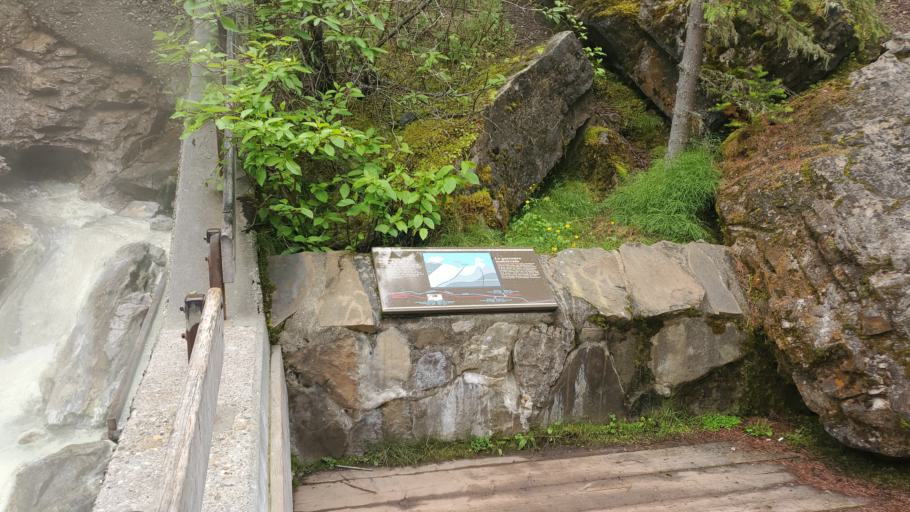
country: CA
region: Alberta
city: Hinton
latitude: 53.1244
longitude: -117.7752
